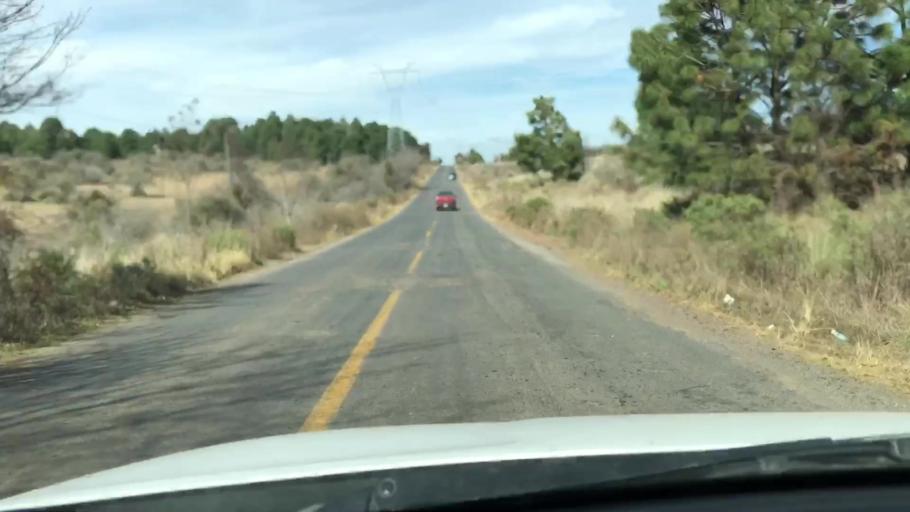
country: MX
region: Jalisco
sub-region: Amacueca
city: Tepec
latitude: 20.1015
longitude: -103.7183
